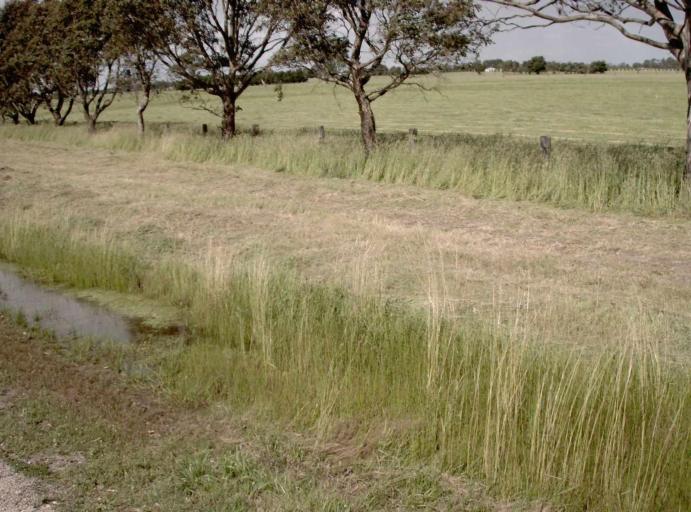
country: AU
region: Victoria
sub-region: Latrobe
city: Traralgon
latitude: -38.1465
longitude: 146.5240
